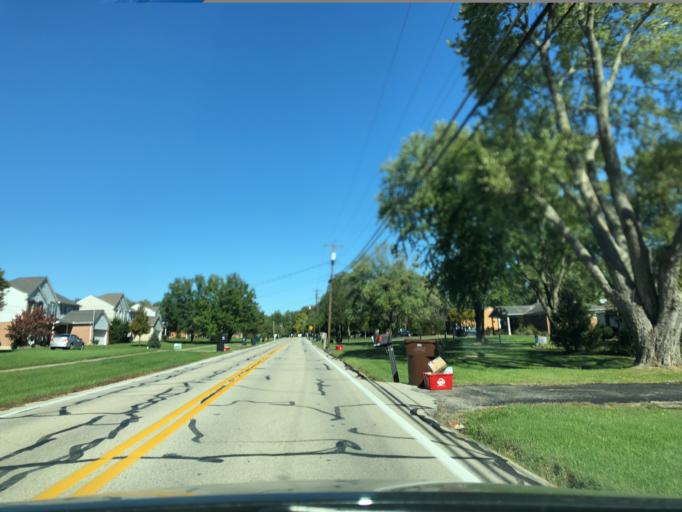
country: US
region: Ohio
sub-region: Hamilton County
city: Sixteen Mile Stand
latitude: 39.2709
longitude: -84.3065
